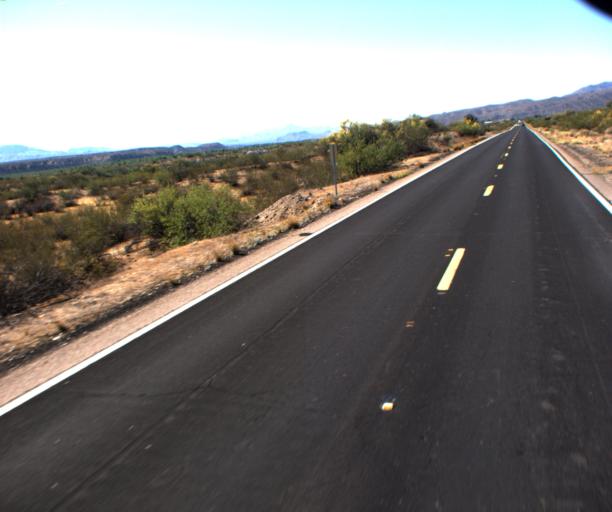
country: US
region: Arizona
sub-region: Yavapai County
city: Bagdad
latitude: 34.7329
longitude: -113.6153
